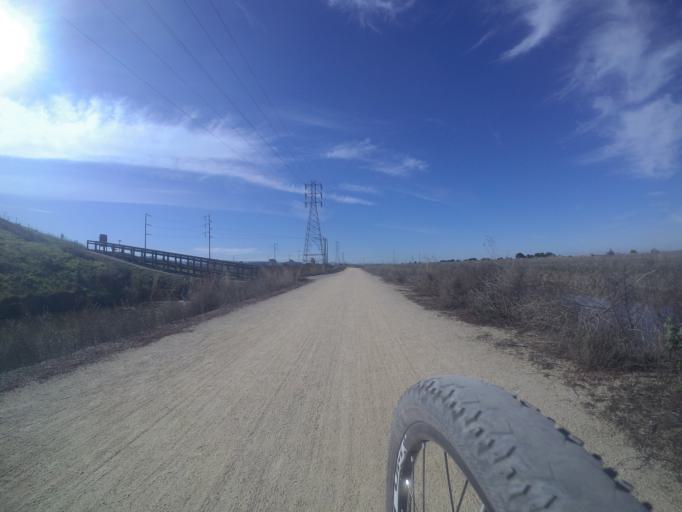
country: US
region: California
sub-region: Santa Clara County
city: Sunnyvale
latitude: 37.4218
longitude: -122.0221
